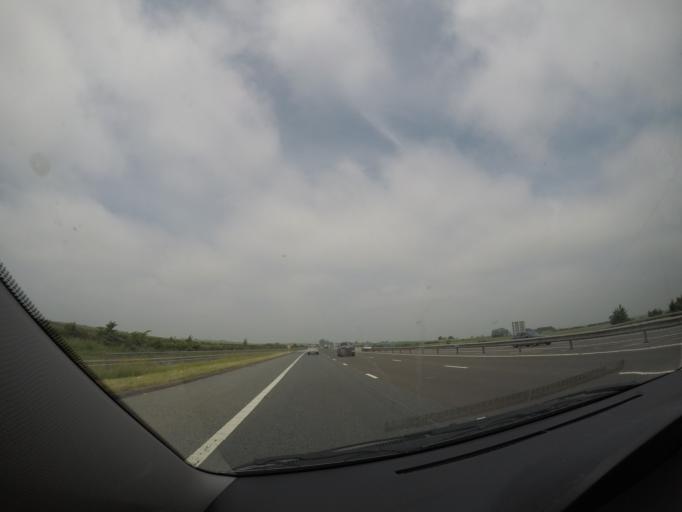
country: GB
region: England
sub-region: North Yorkshire
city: Boroughbridge
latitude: 54.1512
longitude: -1.4374
